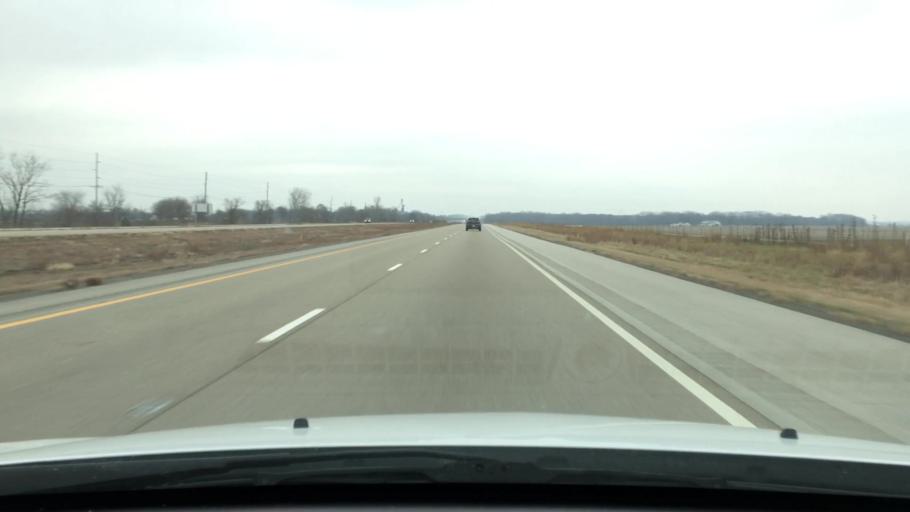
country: US
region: Illinois
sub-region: Logan County
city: Atlanta
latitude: 40.2072
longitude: -89.2932
